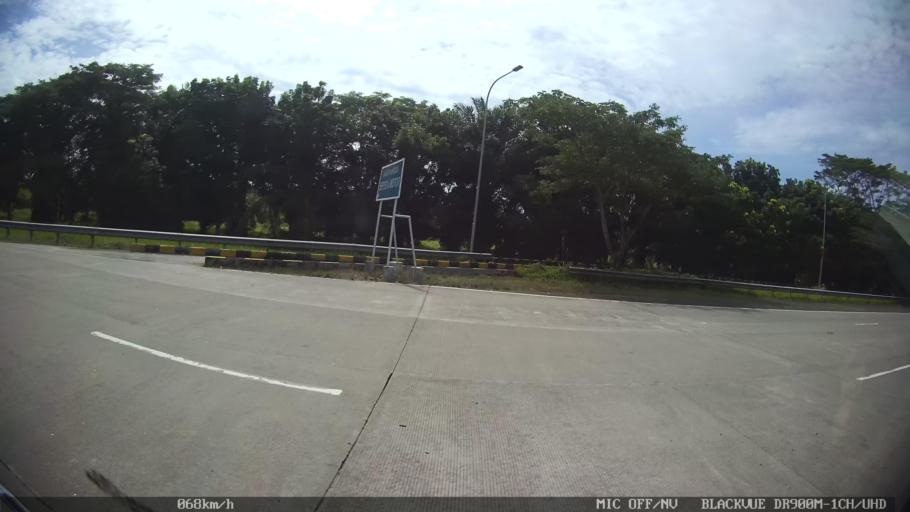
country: ID
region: North Sumatra
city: Percut
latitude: 3.6151
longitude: 98.8593
